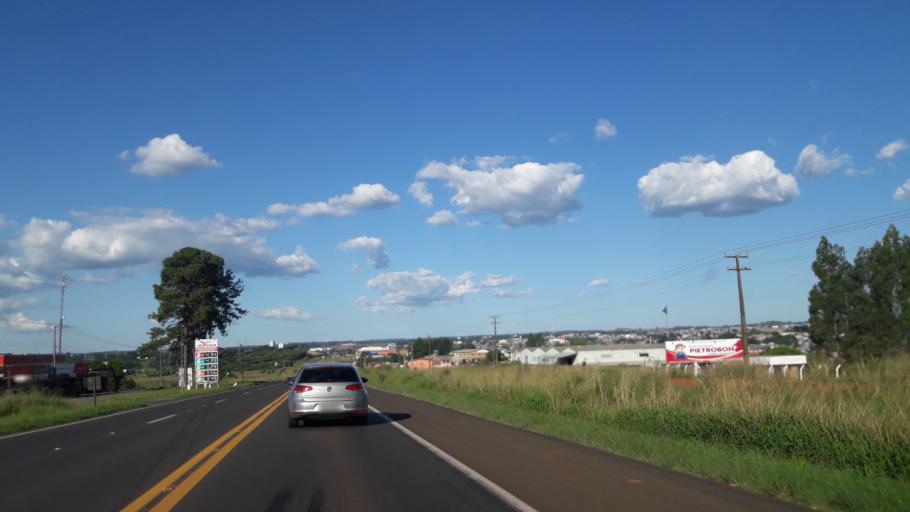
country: BR
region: Parana
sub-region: Guarapuava
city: Guarapuava
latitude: -25.3806
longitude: -51.5091
